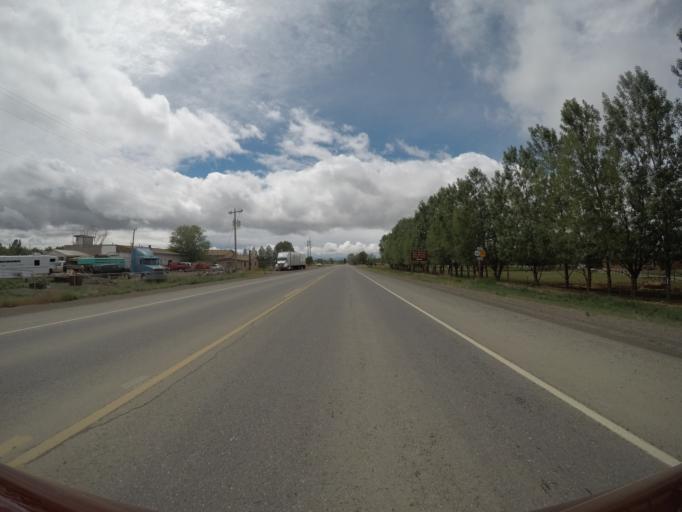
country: US
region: Wyoming
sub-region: Big Horn County
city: Lovell
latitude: 44.8405
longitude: -108.3711
